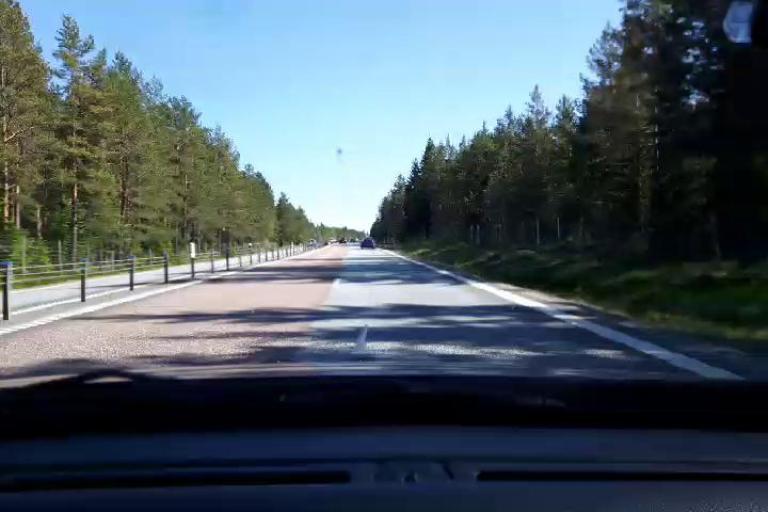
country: SE
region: Gaevleborg
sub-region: Gavle Kommun
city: Norrsundet
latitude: 60.8556
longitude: 17.0659
